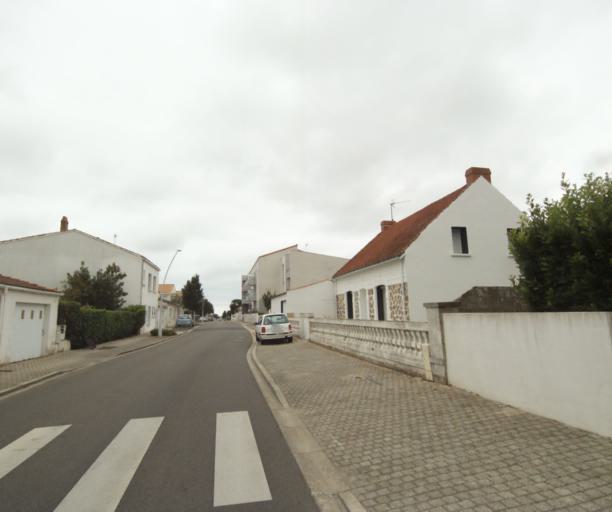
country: FR
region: Pays de la Loire
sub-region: Departement de la Vendee
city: Chateau-d'Olonne
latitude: 46.5035
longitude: -1.7432
